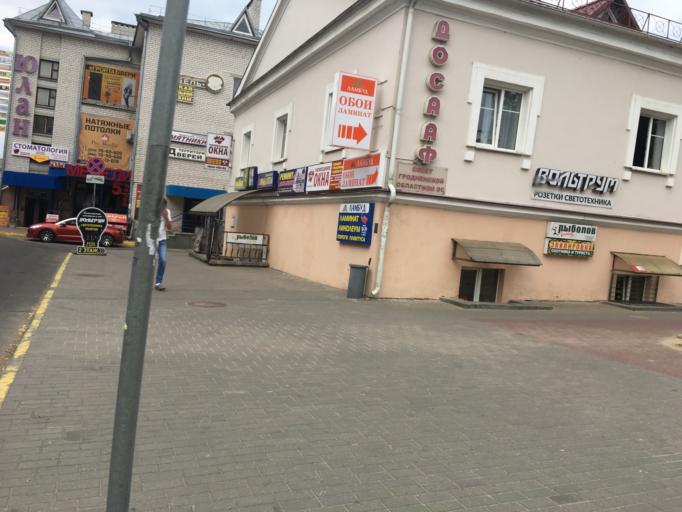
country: BY
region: Grodnenskaya
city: Hrodna
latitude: 53.6761
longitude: 23.8464
